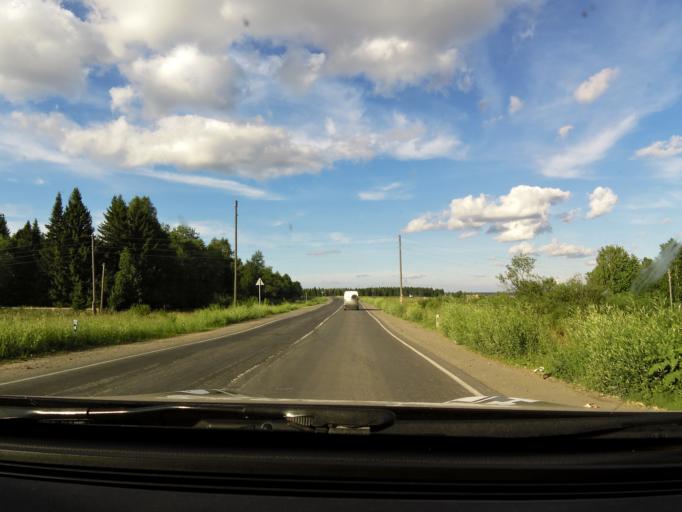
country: RU
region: Kirov
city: Omutninsk
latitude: 58.6901
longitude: 52.1908
